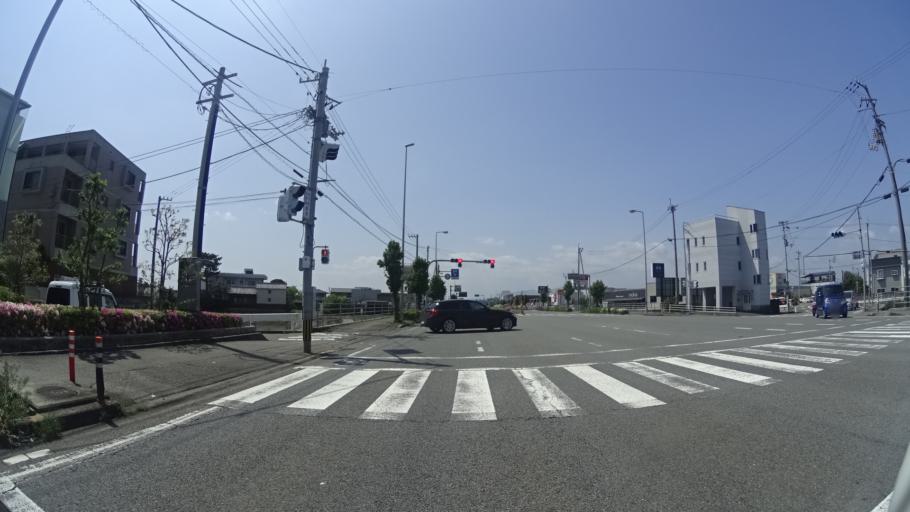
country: JP
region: Tokushima
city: Tokushima-shi
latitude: 34.1087
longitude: 134.5768
